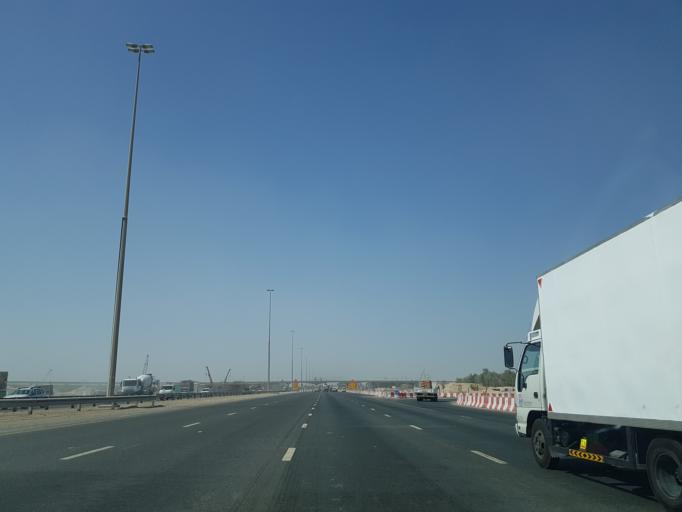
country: AE
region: Dubai
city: Dubai
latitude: 24.9714
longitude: 55.1539
